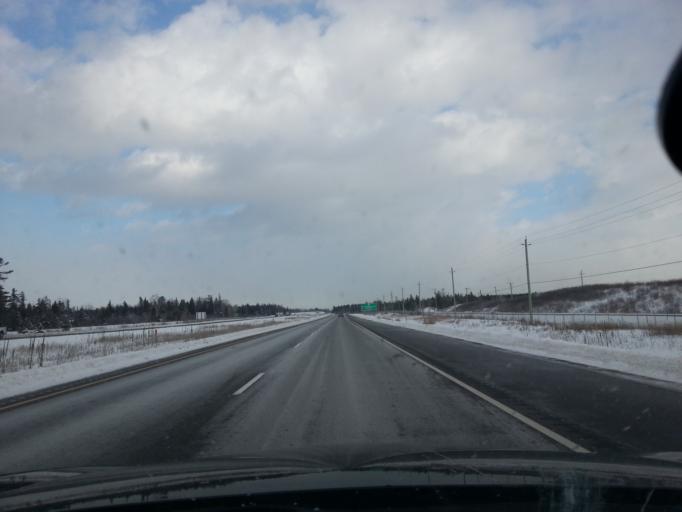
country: CA
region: Ontario
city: Bells Corners
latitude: 45.2375
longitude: -75.9830
